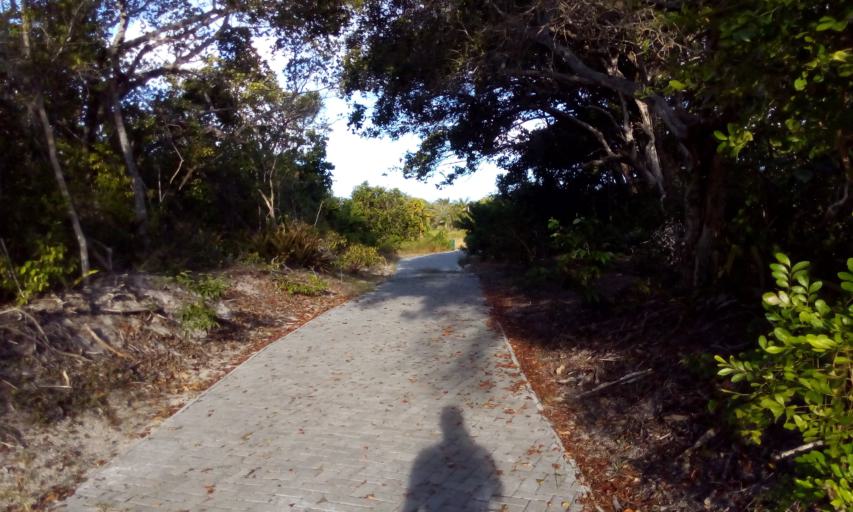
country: BR
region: Bahia
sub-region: Mata De Sao Joao
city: Mata de Sao Joao
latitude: -12.5619
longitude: -38.0000
